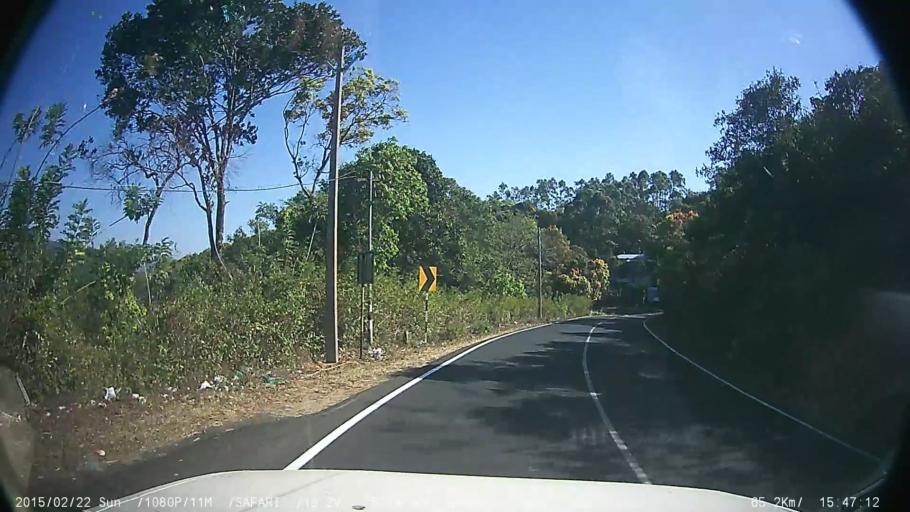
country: IN
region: Kerala
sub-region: Kottayam
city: Erattupetta
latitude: 9.5786
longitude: 76.9893
